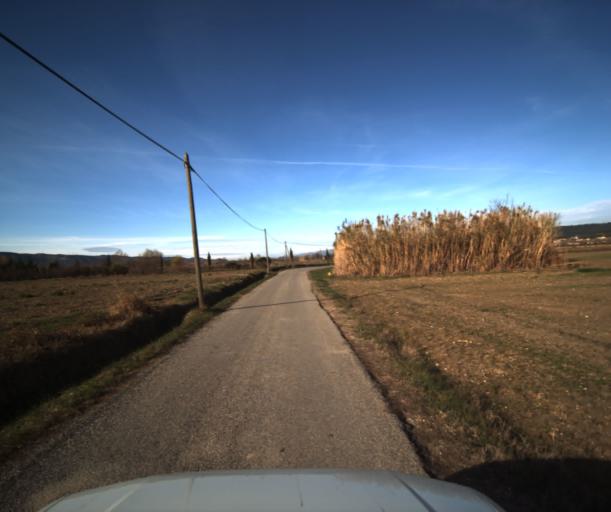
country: FR
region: Provence-Alpes-Cote d'Azur
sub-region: Departement du Vaucluse
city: Villelaure
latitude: 43.6956
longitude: 5.4476
